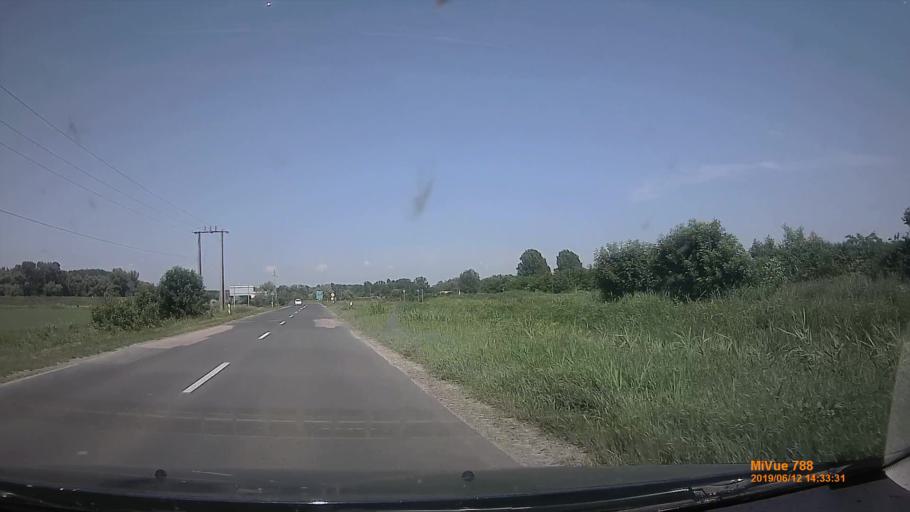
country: HU
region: Csongrad
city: Kiszombor
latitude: 46.1950
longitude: 20.4399
